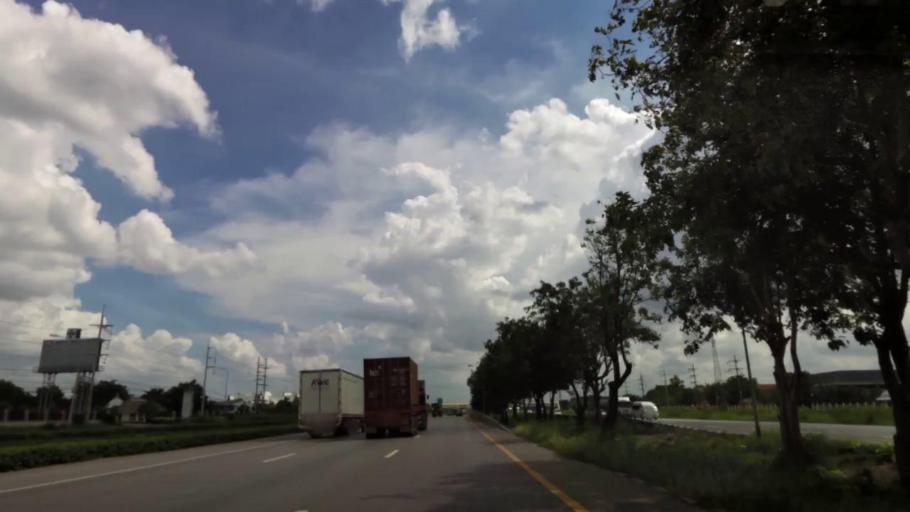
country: TH
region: Phra Nakhon Si Ayutthaya
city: Phra Nakhon Si Ayutthaya
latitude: 14.3820
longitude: 100.6056
